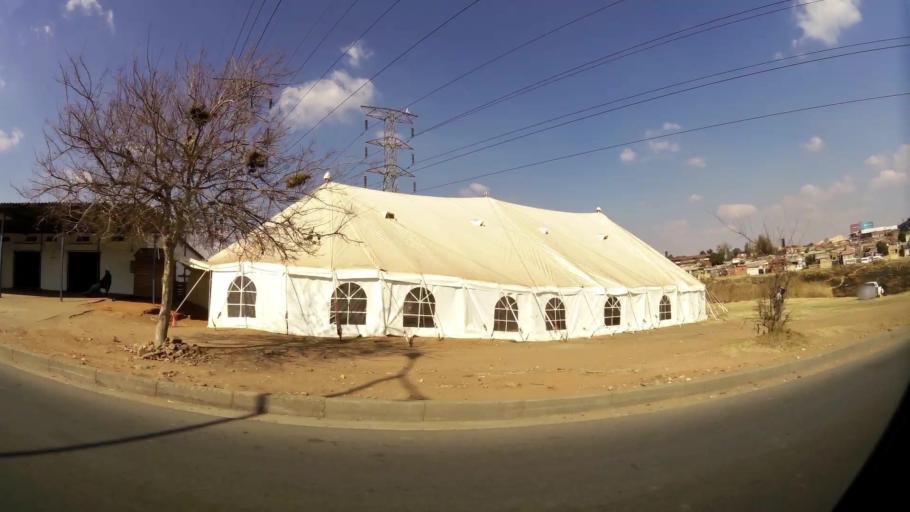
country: ZA
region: Gauteng
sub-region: City of Johannesburg Metropolitan Municipality
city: Soweto
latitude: -26.2543
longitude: 27.9448
